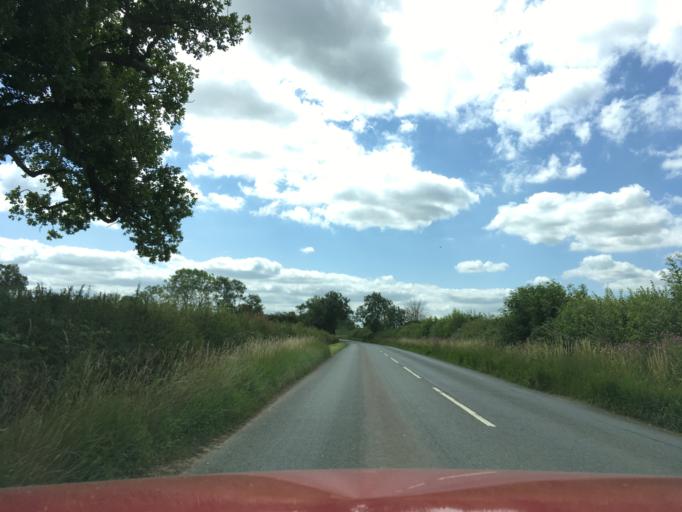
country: GB
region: England
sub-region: Buckinghamshire
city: Newton Longville
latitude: 51.9649
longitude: -0.8164
